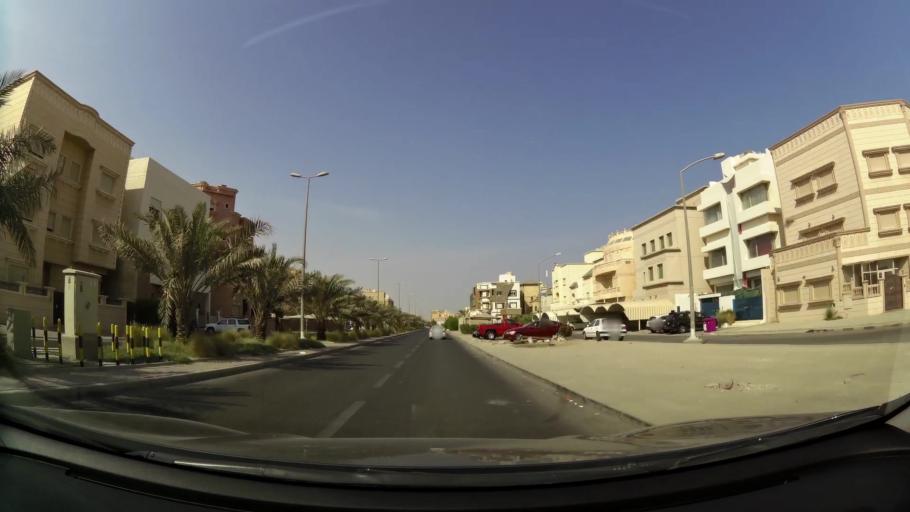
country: KW
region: Al Ahmadi
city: Al Manqaf
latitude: 29.1083
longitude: 48.1238
